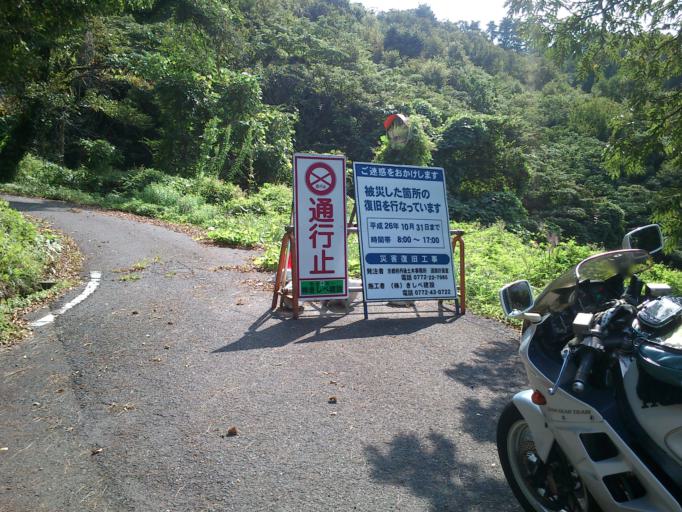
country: JP
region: Kyoto
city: Miyazu
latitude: 35.6557
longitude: 135.2382
